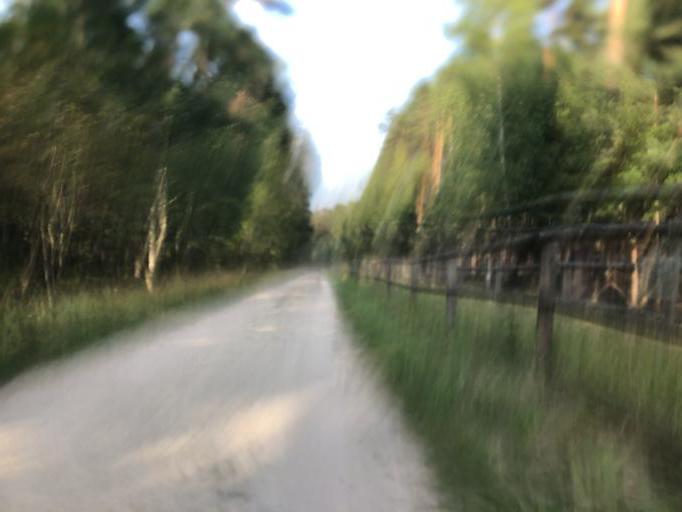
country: DE
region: Bavaria
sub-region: Regierungsbezirk Mittelfranken
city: Buckenhof
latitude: 49.5627
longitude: 11.0626
